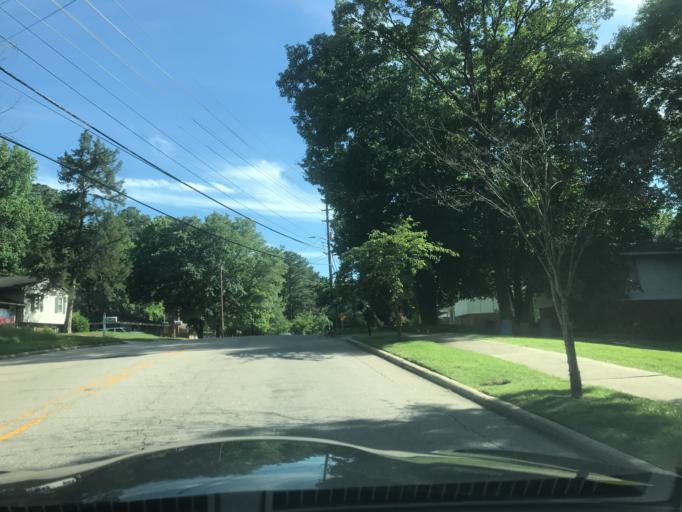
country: US
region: North Carolina
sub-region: Wake County
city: Raleigh
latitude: 35.8300
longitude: -78.6004
